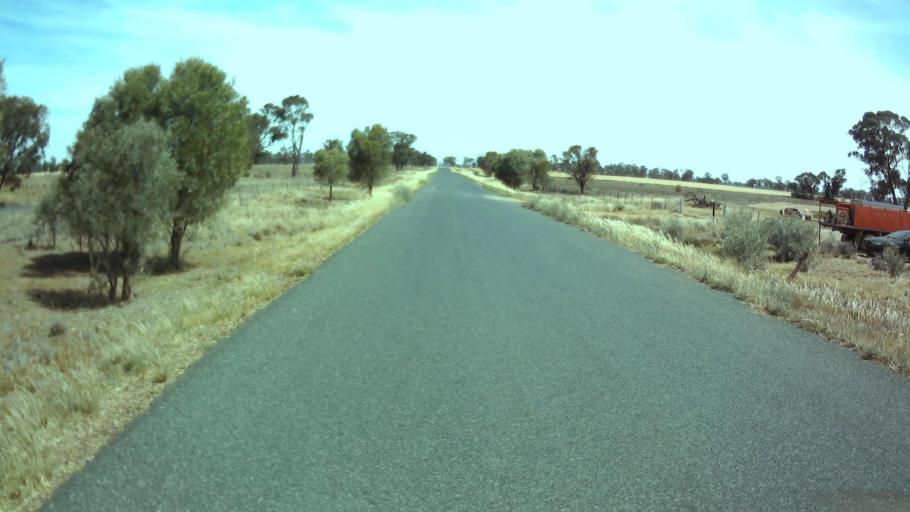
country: AU
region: New South Wales
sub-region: Weddin
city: Grenfell
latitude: -33.9939
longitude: 147.7755
